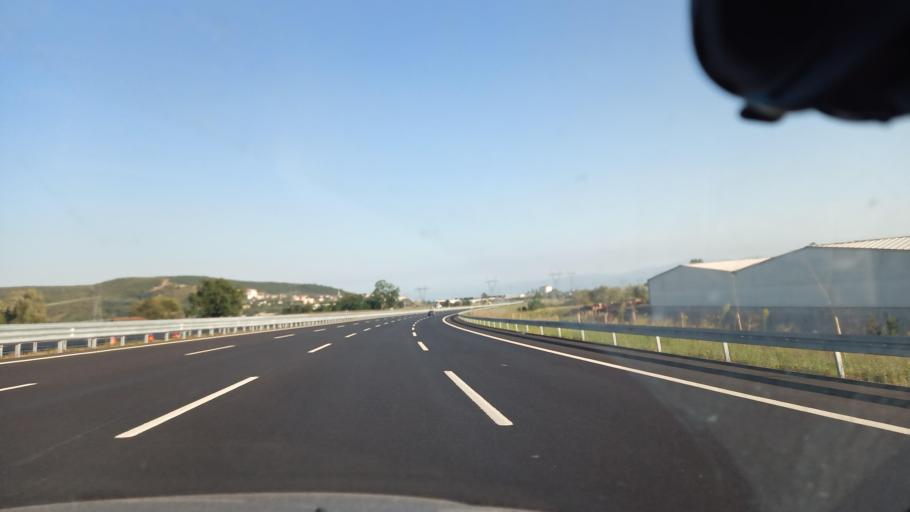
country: TR
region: Sakarya
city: Adapazari
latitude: 40.8366
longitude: 30.3843
